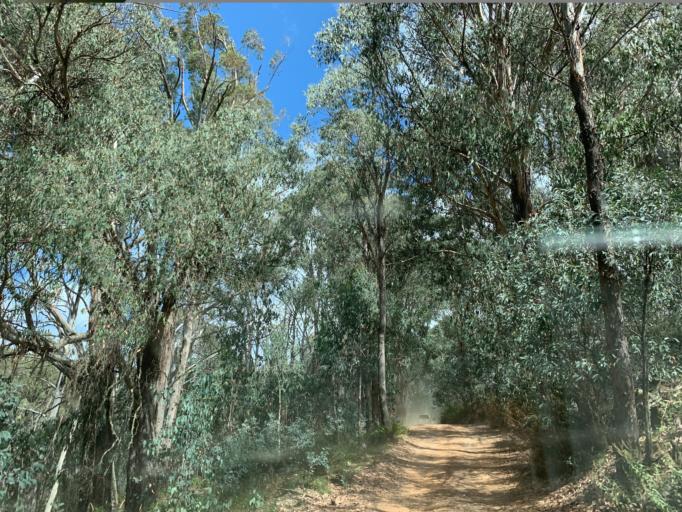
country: AU
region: Victoria
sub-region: Mansfield
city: Mansfield
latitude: -37.1079
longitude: 146.5351
